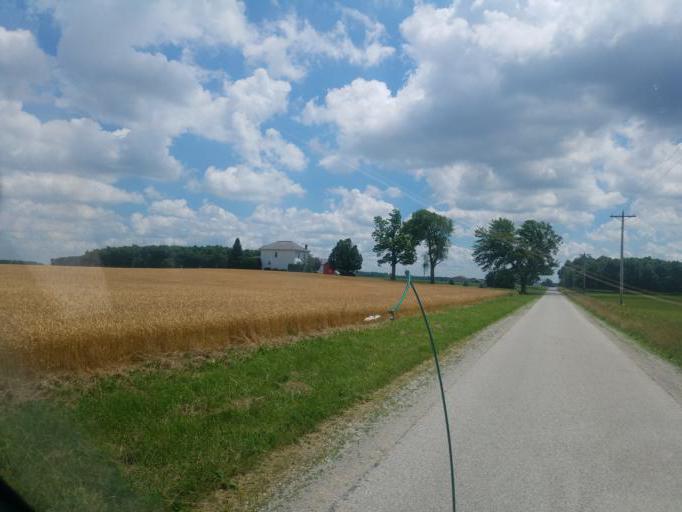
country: US
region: Ohio
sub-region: Huron County
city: Willard
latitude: 41.0150
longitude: -82.8302
